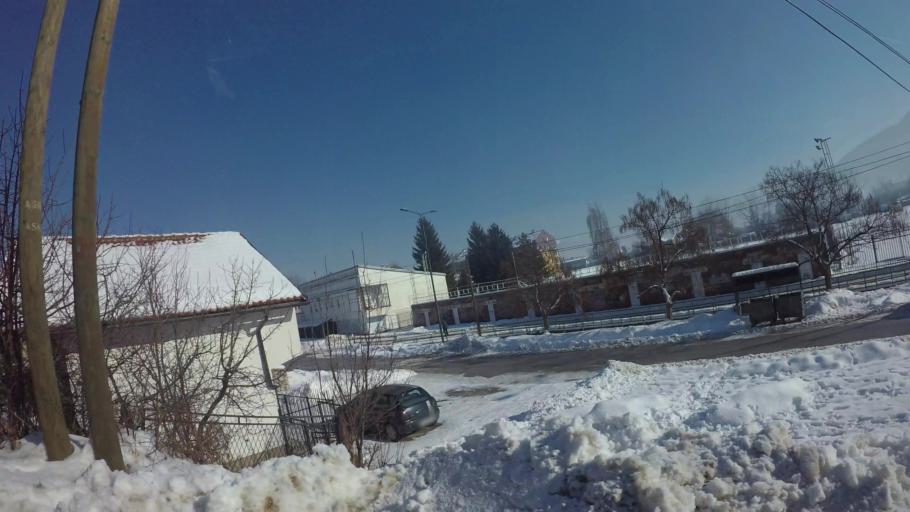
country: BA
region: Federation of Bosnia and Herzegovina
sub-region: Kanton Sarajevo
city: Sarajevo
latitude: 43.7938
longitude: 18.3200
